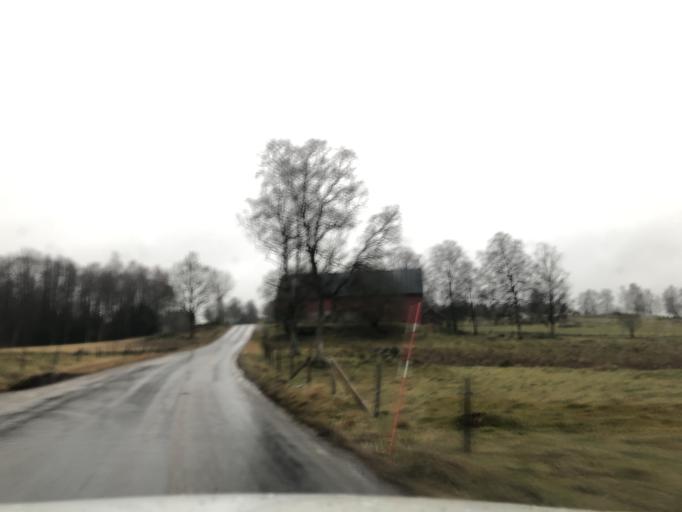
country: SE
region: Vaestra Goetaland
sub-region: Ulricehamns Kommun
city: Ulricehamn
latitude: 57.8522
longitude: 13.5464
